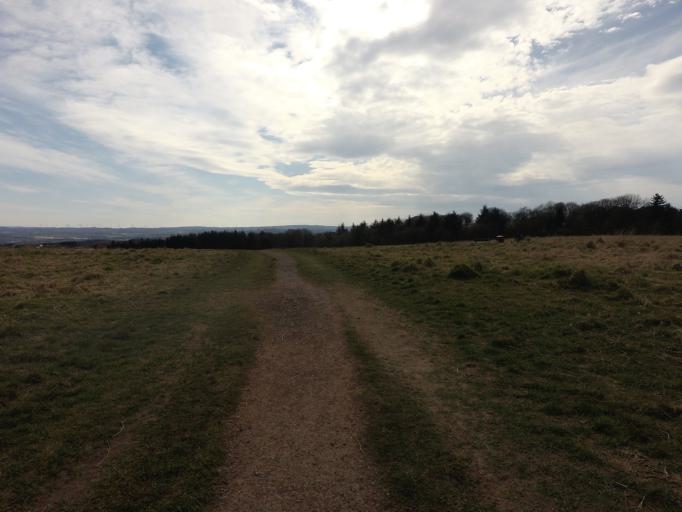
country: GB
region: Scotland
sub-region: West Lothian
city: Livingston
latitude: 55.9109
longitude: -3.5499
